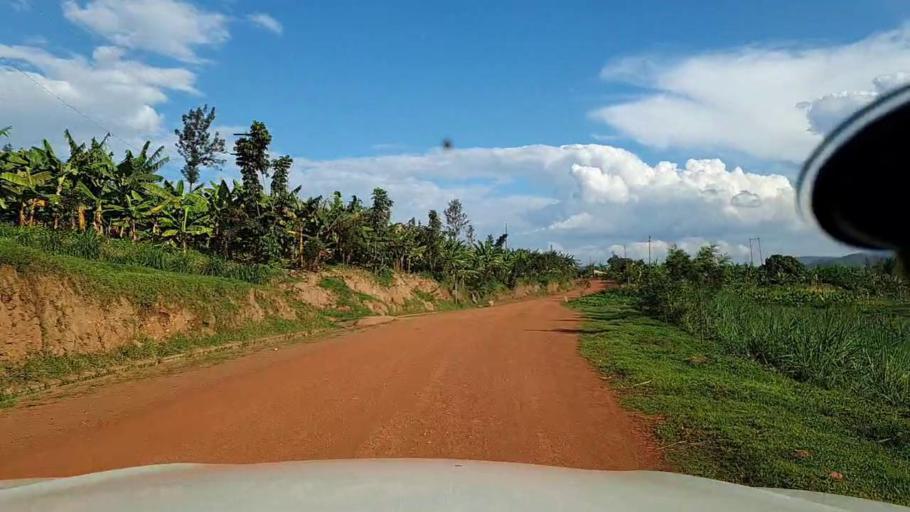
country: RW
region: Kigali
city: Kigali
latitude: -1.8585
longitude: 29.9154
